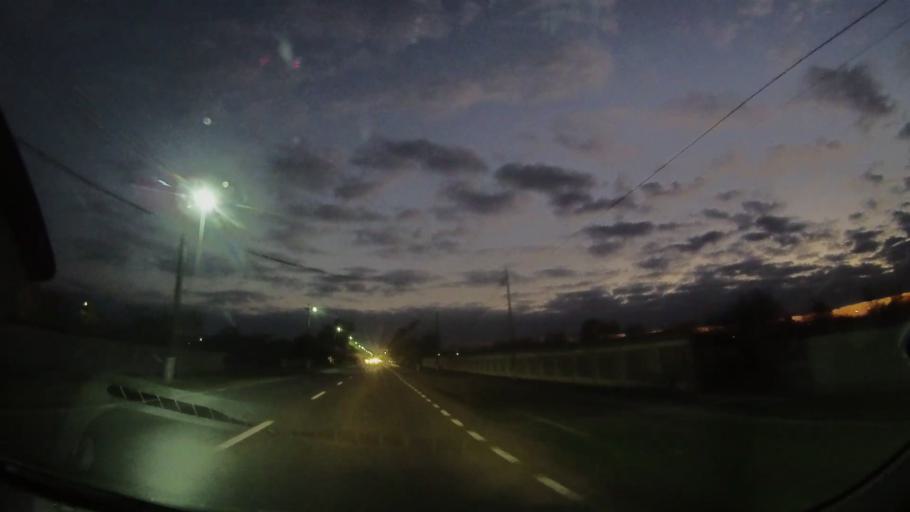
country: RO
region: Tulcea
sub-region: Comuna Mihail Kogalniceanu
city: Mihail Kogalniceanu
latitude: 45.0445
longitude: 28.7357
